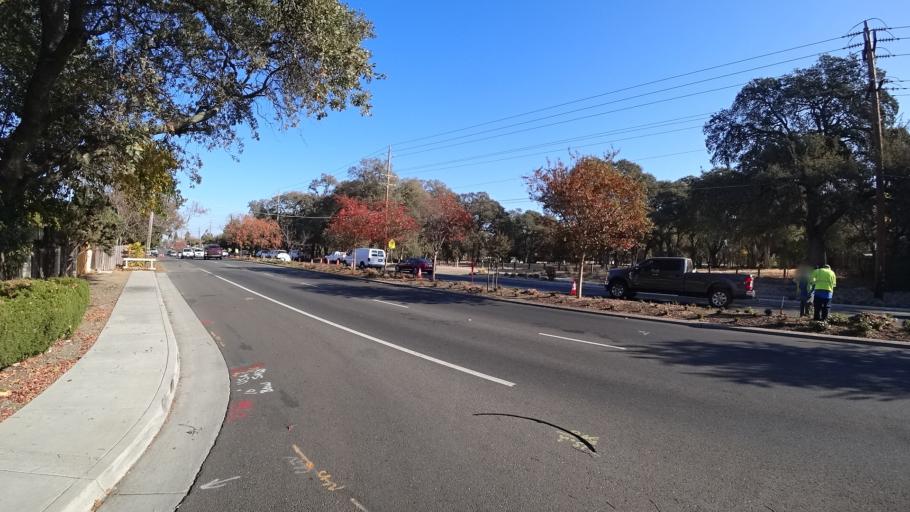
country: US
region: California
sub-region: Sacramento County
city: Citrus Heights
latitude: 38.6968
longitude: -121.2719
